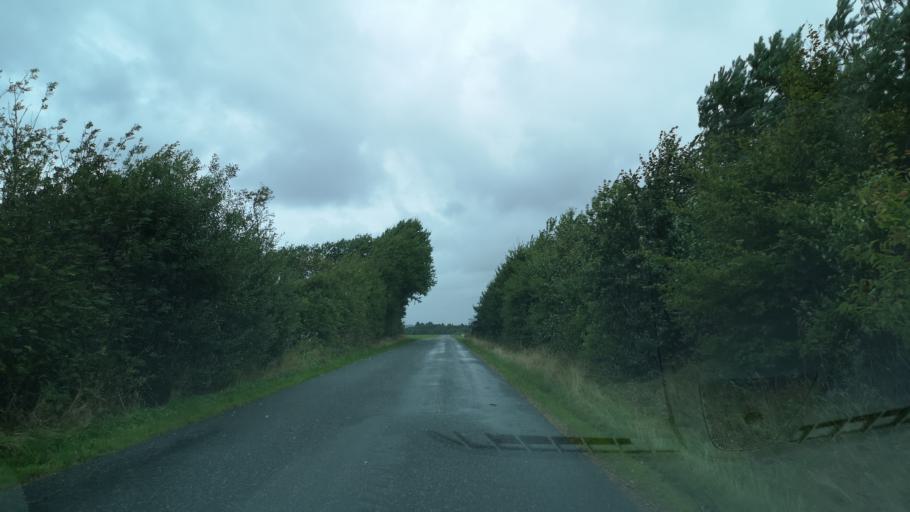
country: DK
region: Central Jutland
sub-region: Ringkobing-Skjern Kommune
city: Videbaek
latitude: 56.0622
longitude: 8.6719
